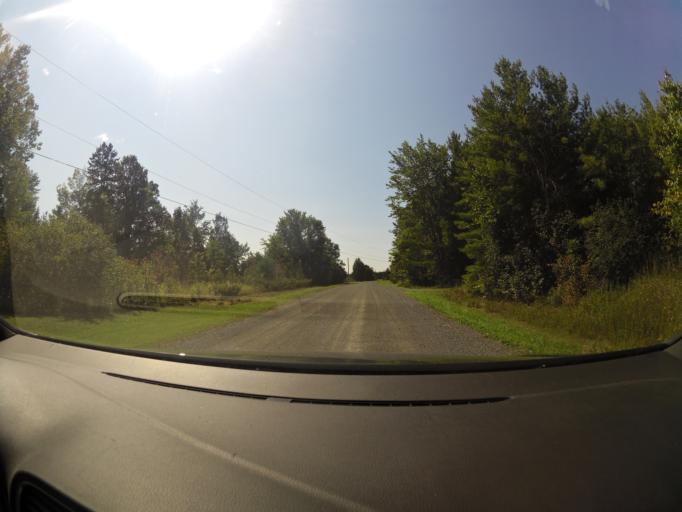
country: CA
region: Ontario
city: Arnprior
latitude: 45.3104
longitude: -76.2585
